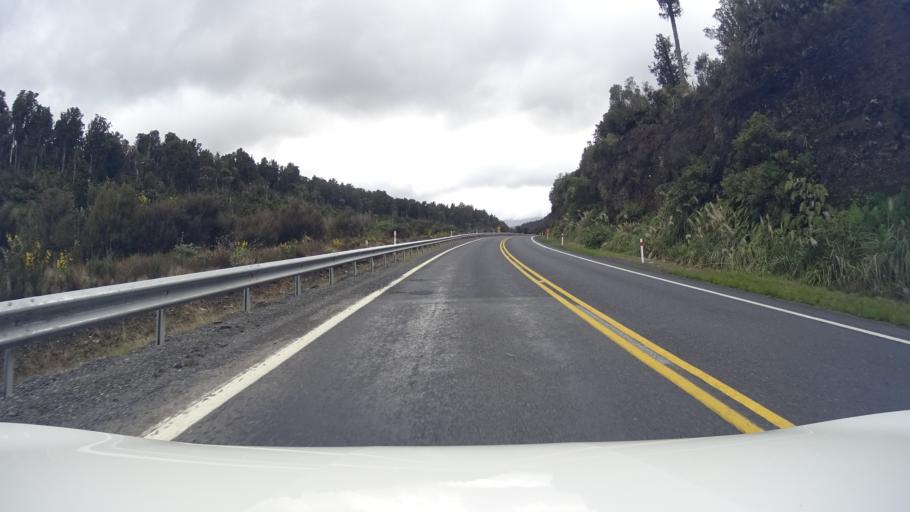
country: NZ
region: Manawatu-Wanganui
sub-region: Ruapehu District
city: Waiouru
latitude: -39.2651
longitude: 175.3944
